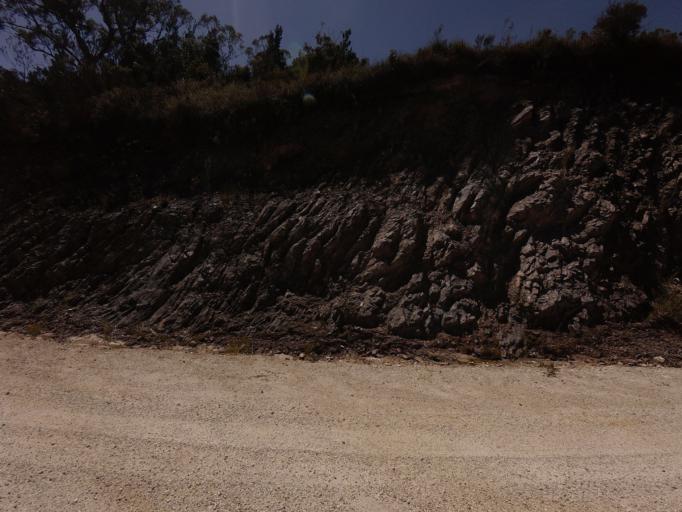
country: AU
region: Tasmania
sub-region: Huon Valley
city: Geeveston
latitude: -42.9316
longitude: 146.3418
